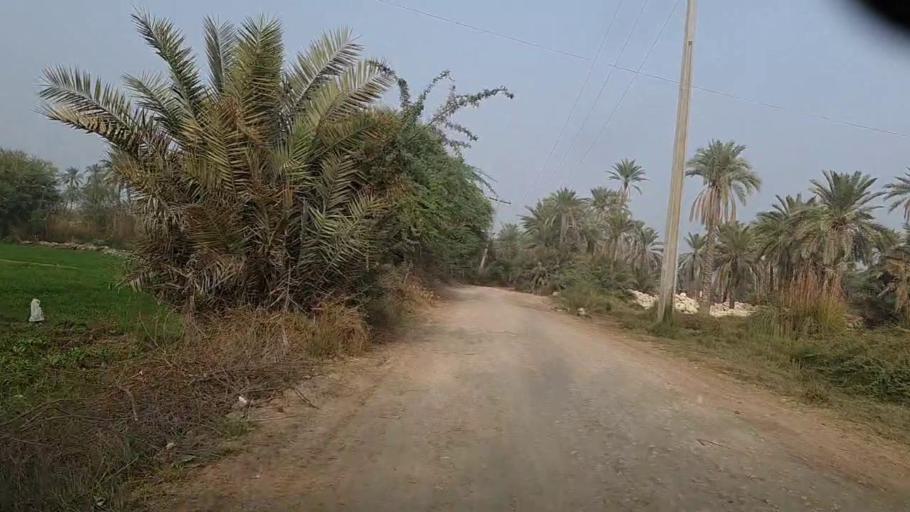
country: PK
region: Sindh
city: Bozdar
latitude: 27.1438
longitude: 68.6475
